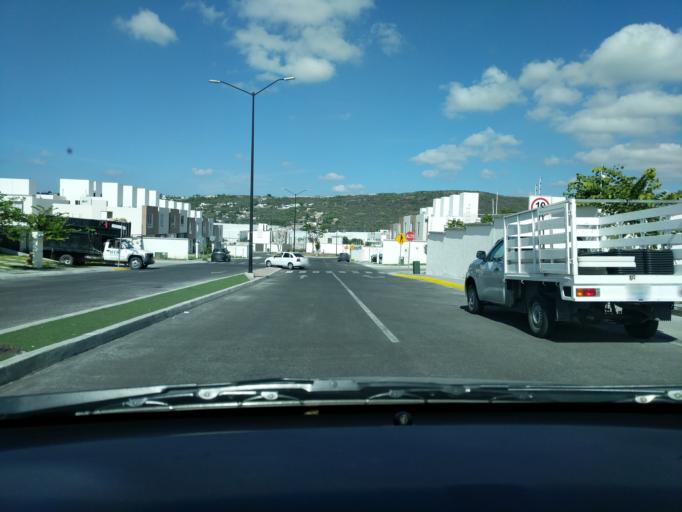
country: MX
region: Queretaro
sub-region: Queretaro
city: Patria Nueva
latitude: 20.6397
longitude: -100.4923
